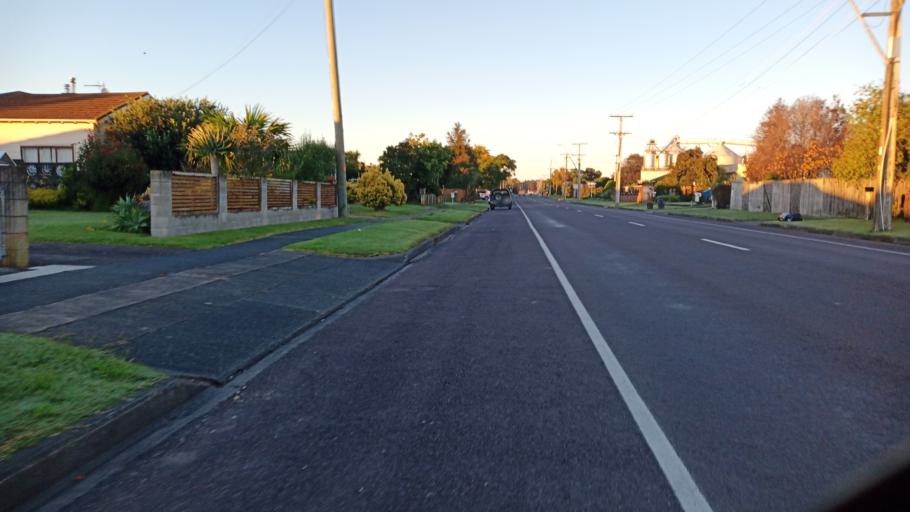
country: NZ
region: Gisborne
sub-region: Gisborne District
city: Gisborne
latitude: -38.6559
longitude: 177.9886
